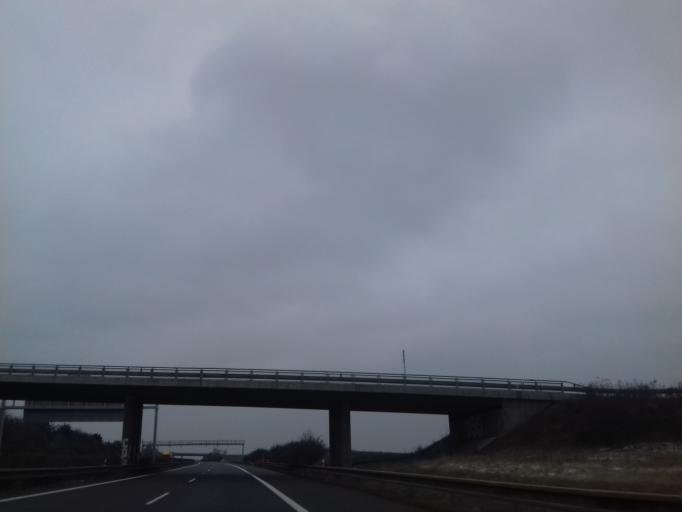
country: CZ
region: Plzensky
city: Stenovice
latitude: 49.6838
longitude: 13.3536
